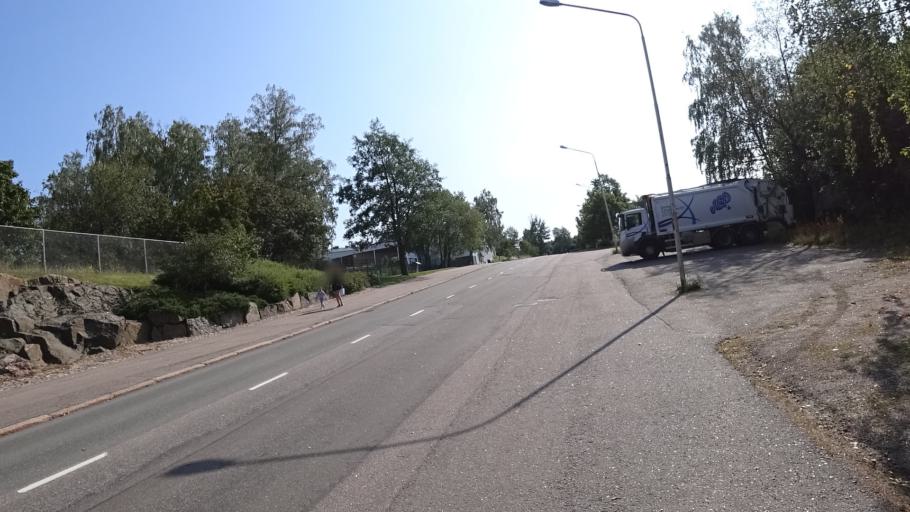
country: FI
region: Kymenlaakso
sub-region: Kotka-Hamina
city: Kotka
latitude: 60.4566
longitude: 26.9369
